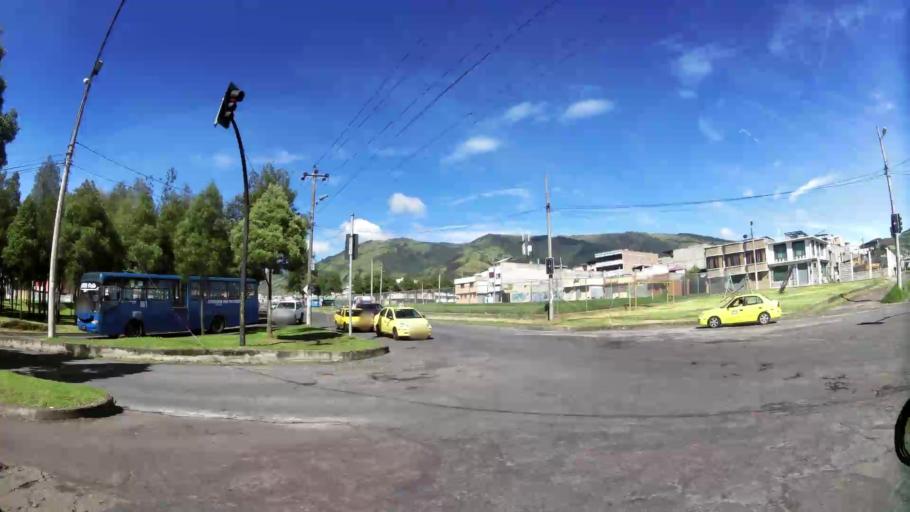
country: EC
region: Pichincha
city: Quito
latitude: -0.2903
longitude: -78.5614
